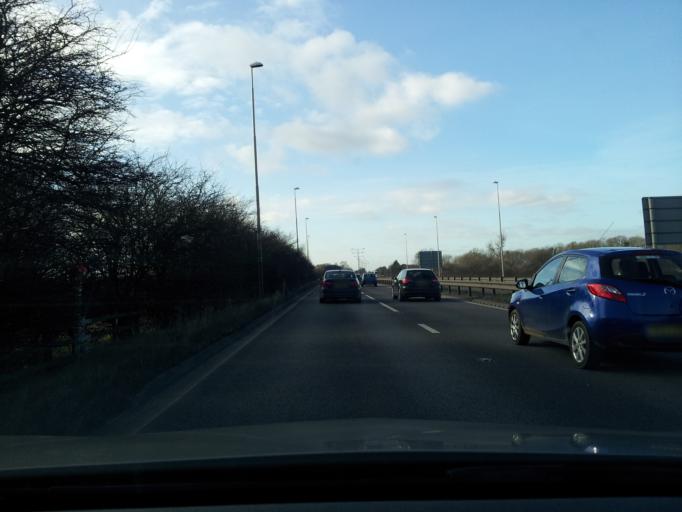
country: GB
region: England
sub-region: Nottinghamshire
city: Radcliffe on Trent
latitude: 52.9369
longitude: -1.0672
